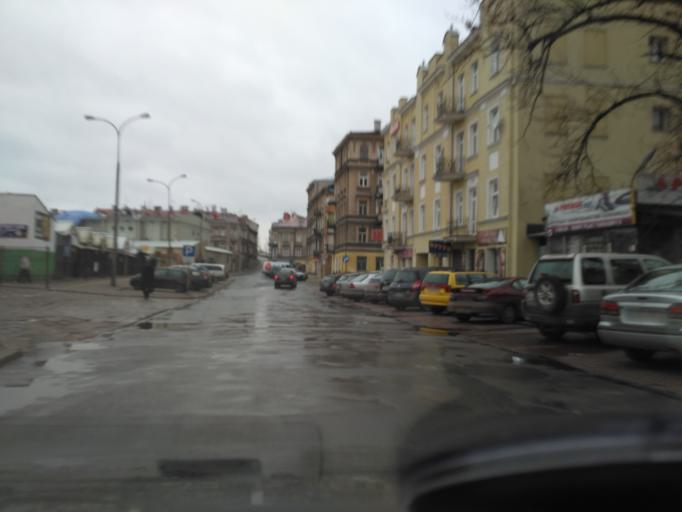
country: PL
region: Lublin Voivodeship
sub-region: Powiat lubelski
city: Lublin
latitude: 51.2524
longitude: 22.5705
